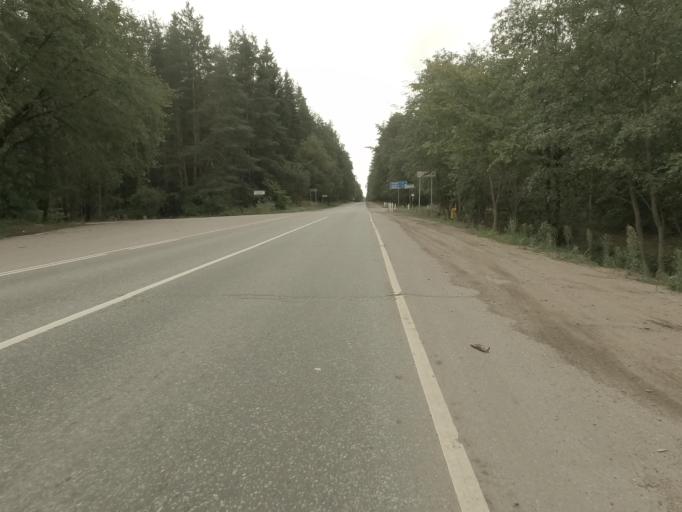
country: RU
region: Leningrad
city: Koltushi
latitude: 59.8932
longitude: 30.7436
